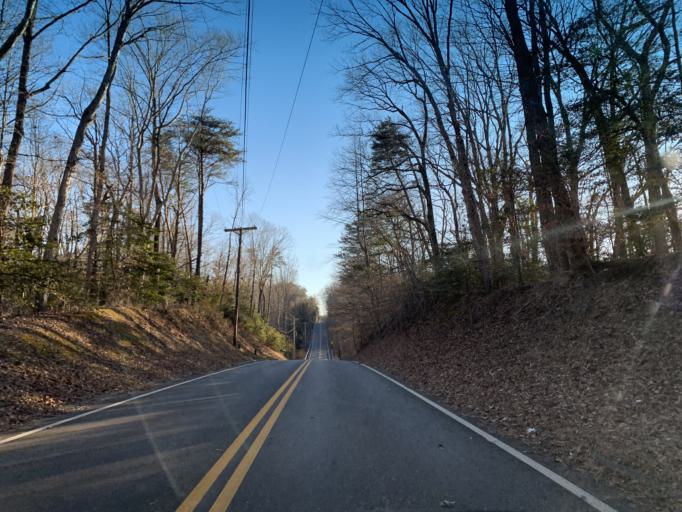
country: US
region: Maryland
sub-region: Saint Mary's County
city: Golden Beach
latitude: 38.4459
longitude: -76.6795
